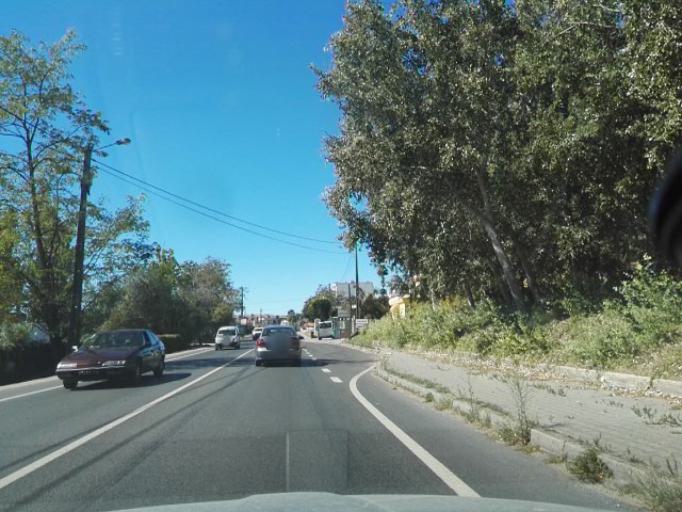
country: PT
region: Lisbon
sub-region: Vila Franca de Xira
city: Sobralinho
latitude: 38.9197
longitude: -9.0174
